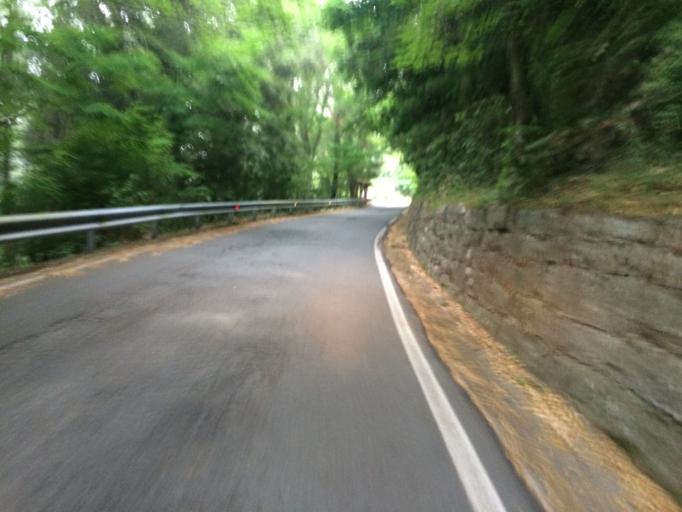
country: IT
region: Liguria
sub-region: Provincia di Imperia
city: Seborga
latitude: 43.8544
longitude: 7.7291
